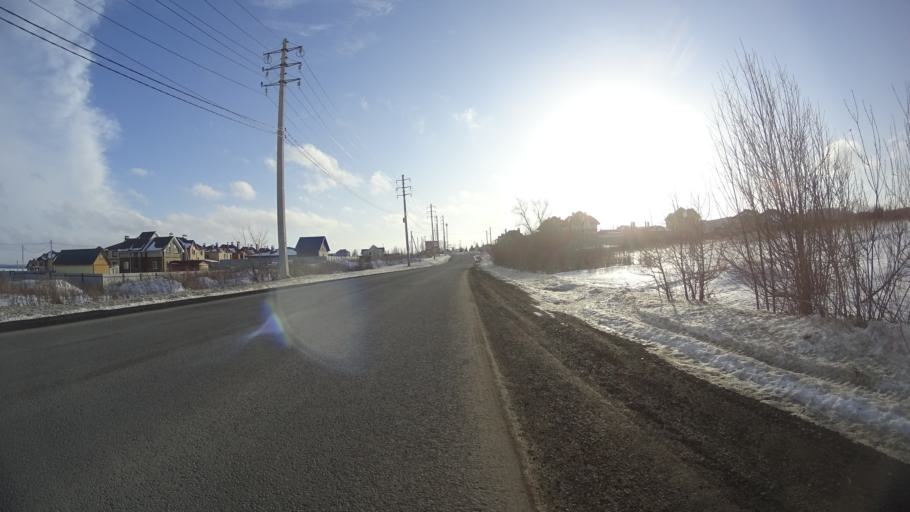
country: RU
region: Chelyabinsk
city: Sargazy
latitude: 55.1177
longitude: 61.2854
